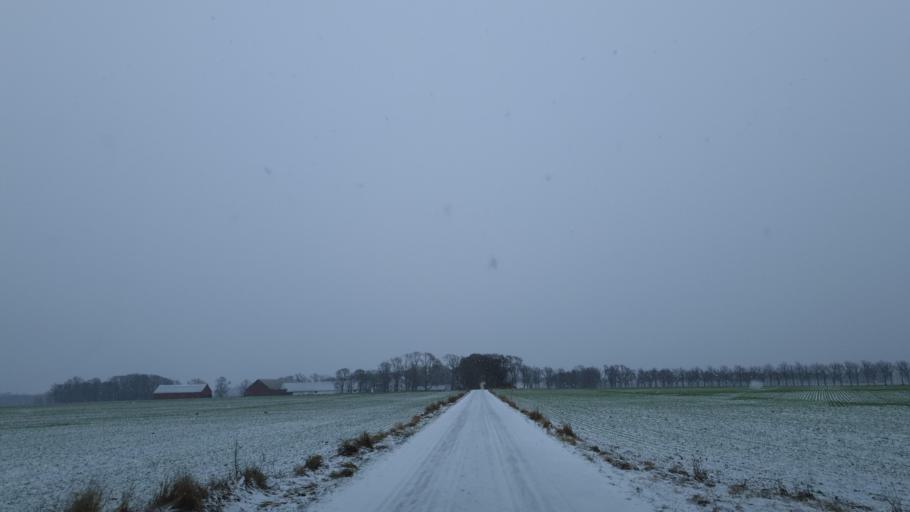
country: SE
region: Gotland
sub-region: Gotland
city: Visby
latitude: 57.5196
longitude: 18.4542
